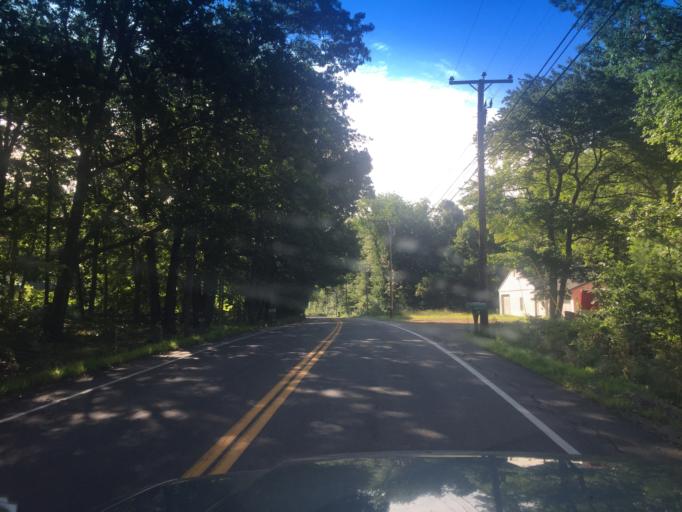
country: US
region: Maine
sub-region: York County
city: South Berwick
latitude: 43.2062
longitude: -70.7787
